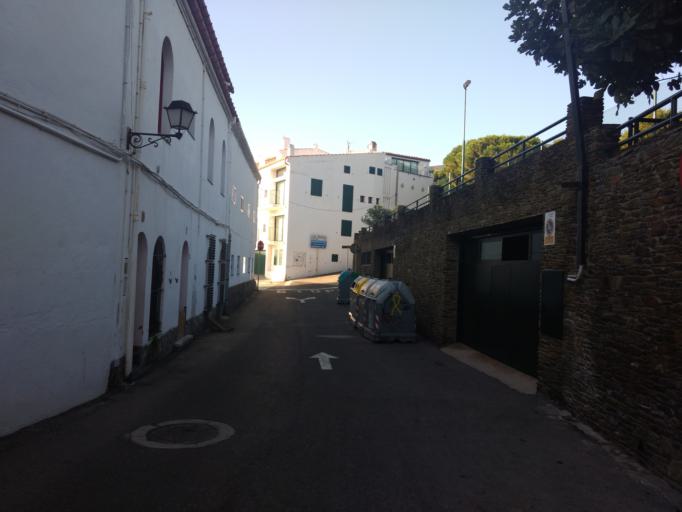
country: ES
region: Catalonia
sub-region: Provincia de Girona
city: Cadaques
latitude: 42.2855
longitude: 3.2759
